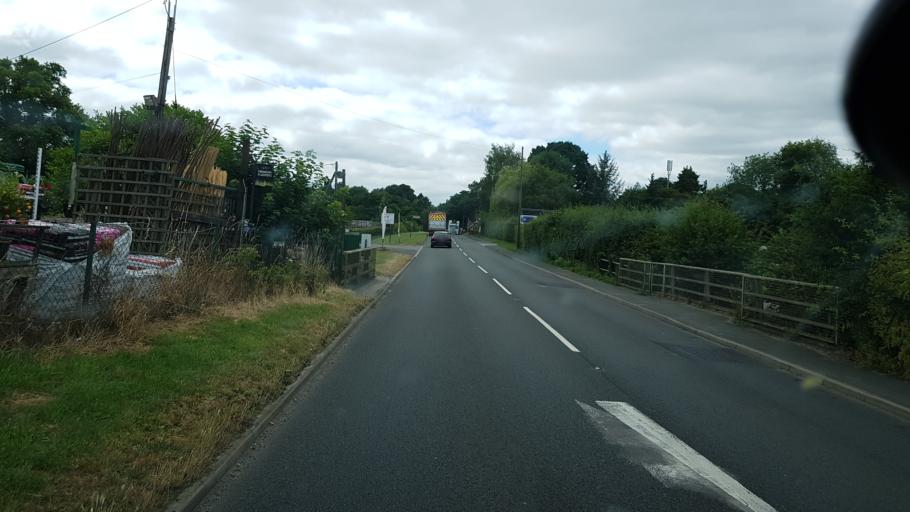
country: GB
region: England
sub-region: Surrey
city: Godstone
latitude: 51.2151
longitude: -0.0515
